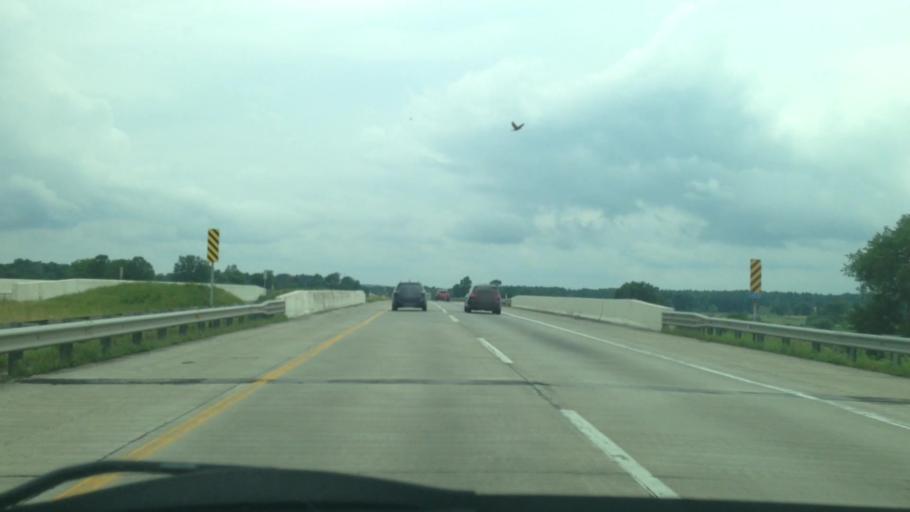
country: US
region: Indiana
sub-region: Steuben County
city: Fremont
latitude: 41.7124
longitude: -84.9441
